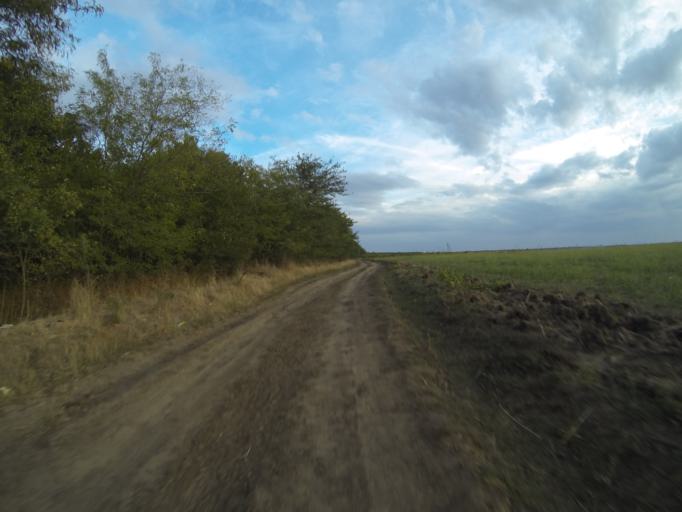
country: RO
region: Dolj
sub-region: Comuna Ceratu
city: Ceratu
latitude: 44.0934
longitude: 23.6720
